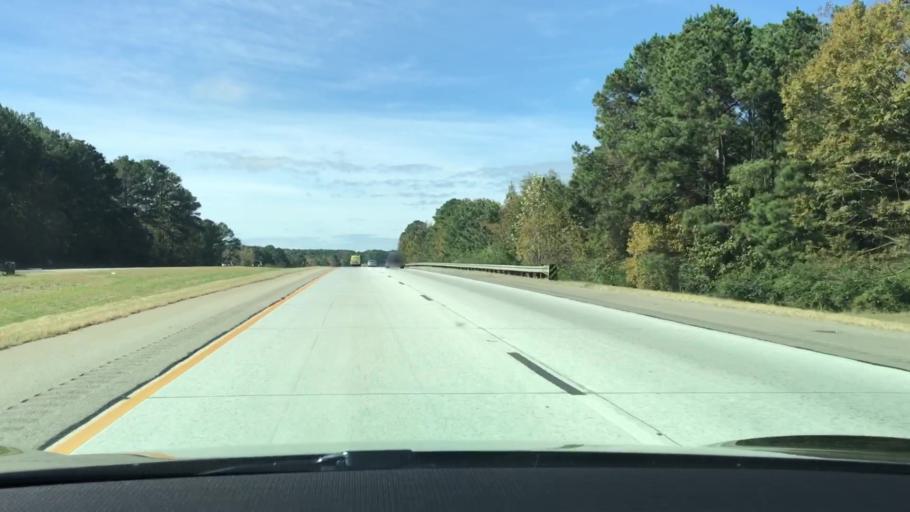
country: US
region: Georgia
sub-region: Greene County
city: Greensboro
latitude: 33.5385
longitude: -83.2366
